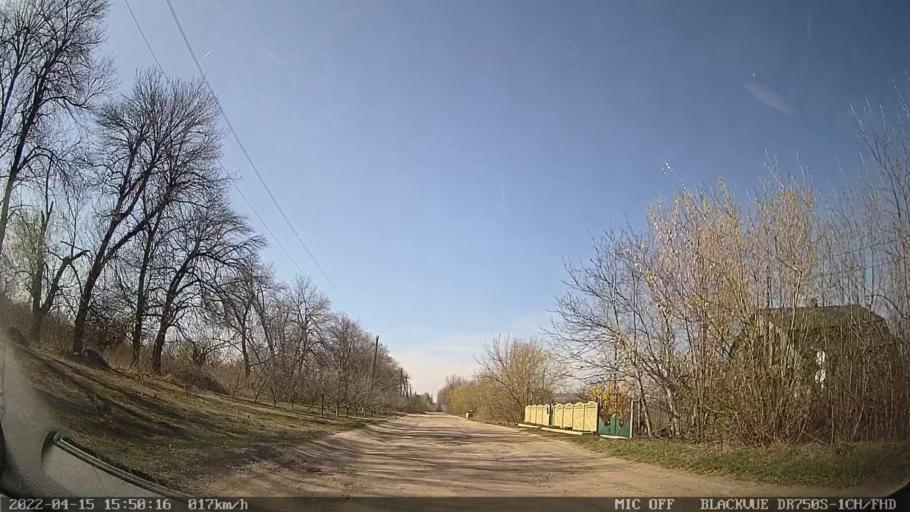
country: MD
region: Raionul Ocnita
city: Otaci
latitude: 48.3913
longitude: 27.9016
